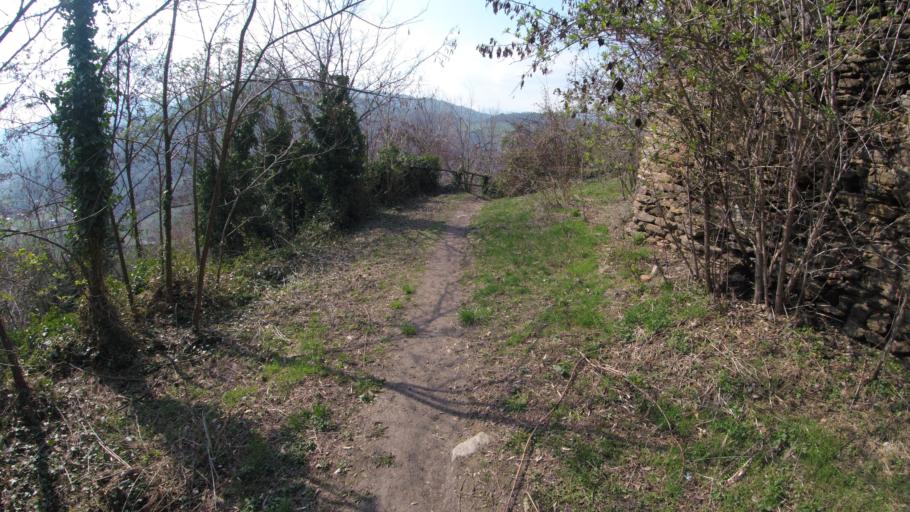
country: IT
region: Piedmont
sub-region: Provincia di Cuneo
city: Rossana
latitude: 44.5403
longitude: 7.4367
